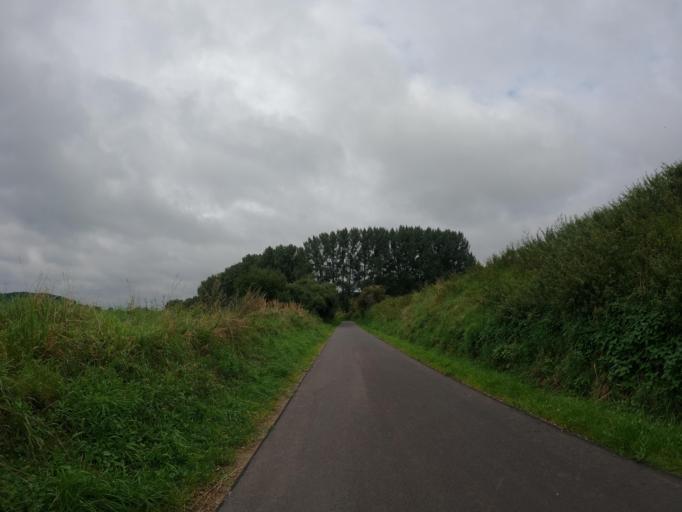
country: DE
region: Mecklenburg-Vorpommern
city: Rambin
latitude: 54.2966
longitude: 13.2145
